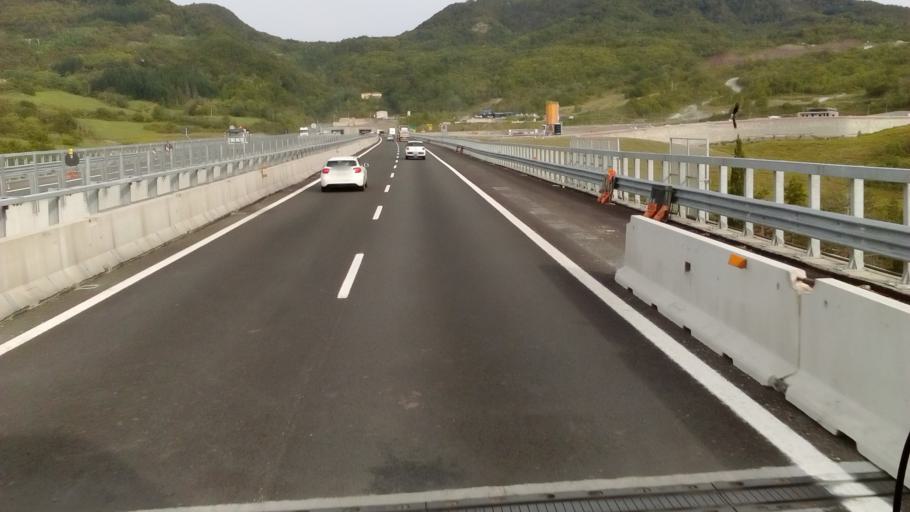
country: IT
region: Tuscany
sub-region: Province of Florence
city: Barberino di Mugello
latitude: 44.0644
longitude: 11.2440
